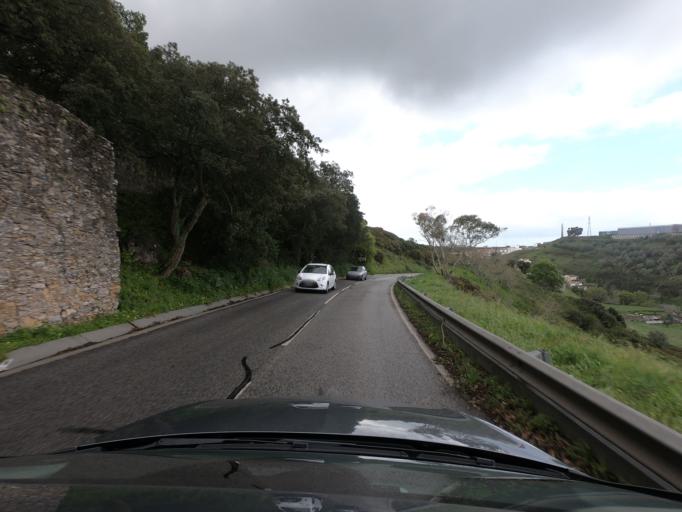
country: PT
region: Lisbon
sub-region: Sintra
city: Queluz
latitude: 38.7423
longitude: -9.2626
